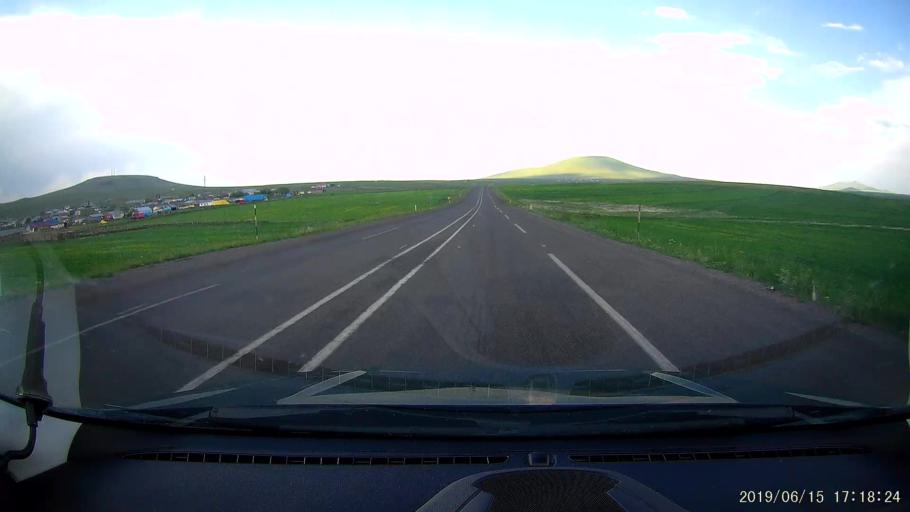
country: TR
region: Kars
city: Kars
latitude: 40.6129
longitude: 43.2569
